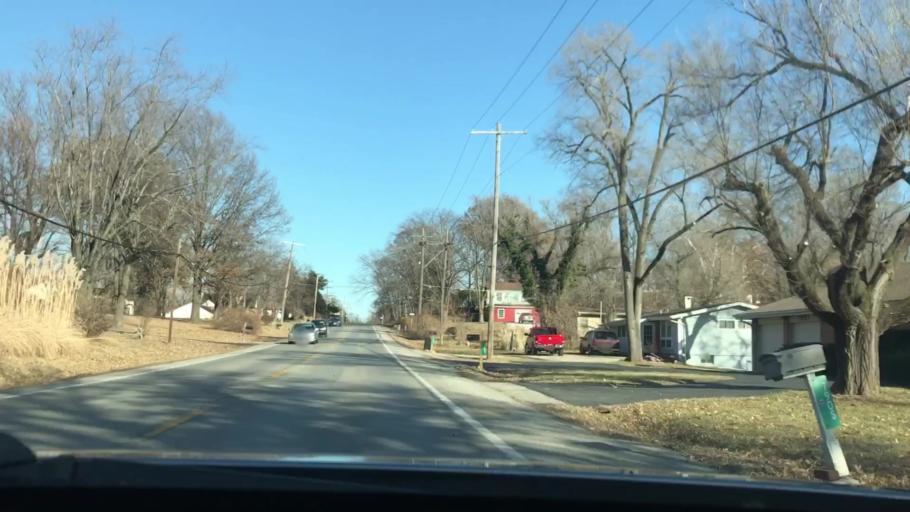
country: US
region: Missouri
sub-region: Platte County
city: Parkville
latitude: 39.2164
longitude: -94.6724
